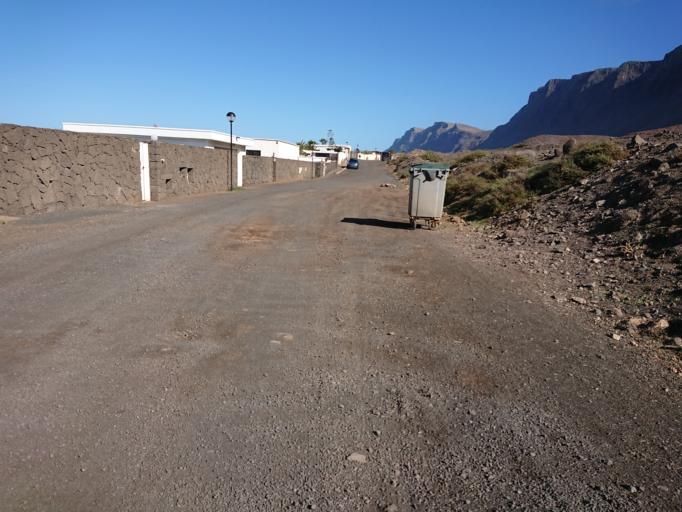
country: ES
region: Canary Islands
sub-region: Provincia de Las Palmas
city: Teguise
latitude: 29.1123
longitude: -13.5451
